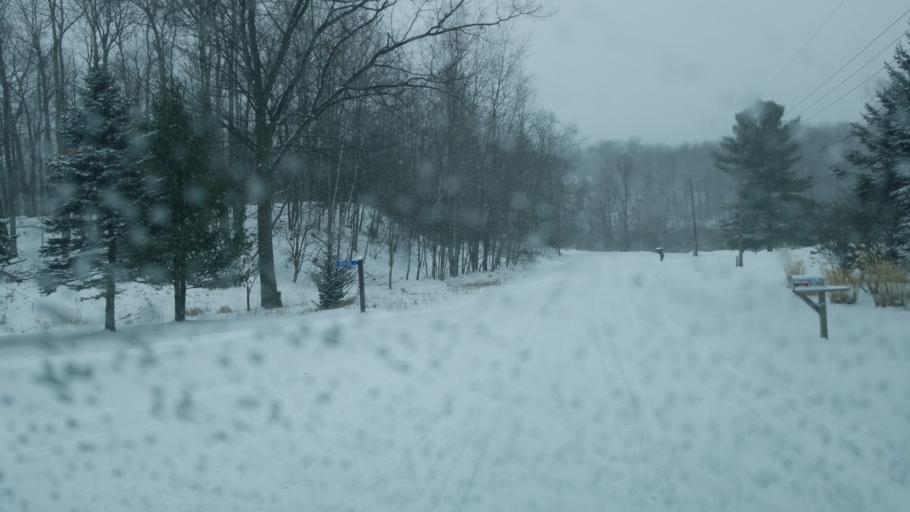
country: US
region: Michigan
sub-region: Mecosta County
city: Canadian Lakes
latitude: 43.6037
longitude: -85.3030
